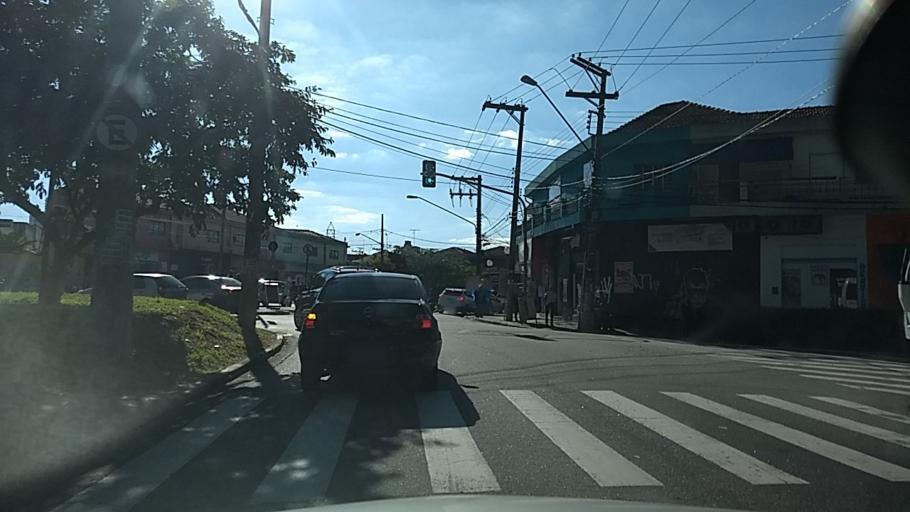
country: BR
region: Sao Paulo
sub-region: Guarulhos
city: Guarulhos
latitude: -23.4923
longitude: -46.5742
